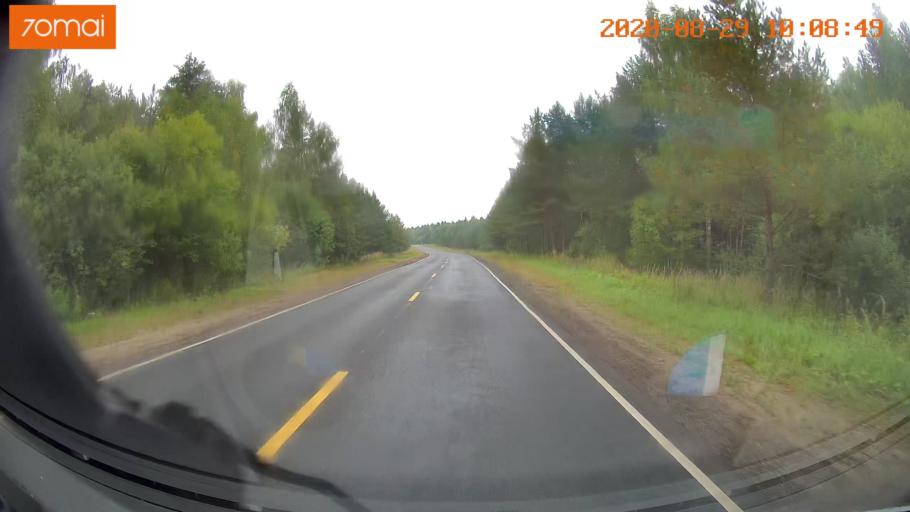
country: RU
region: Ivanovo
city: Kuznechikha
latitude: 57.3746
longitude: 42.5999
